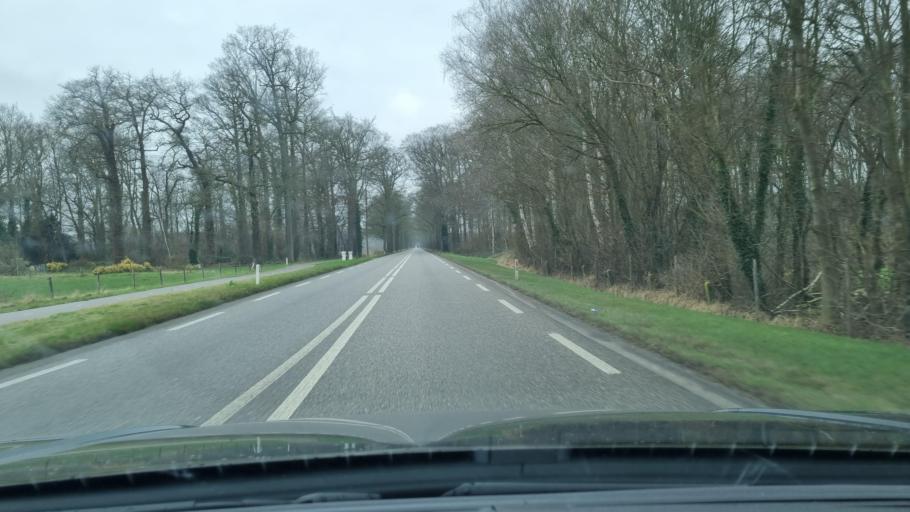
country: NL
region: Gelderland
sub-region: Gemeente Bronckhorst
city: Baak
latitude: 52.0140
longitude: 6.2274
